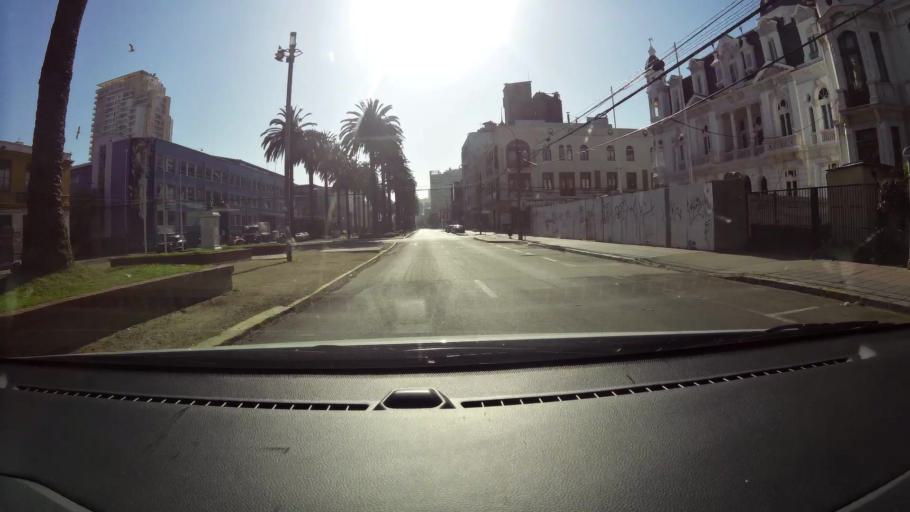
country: CL
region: Valparaiso
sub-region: Provincia de Valparaiso
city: Valparaiso
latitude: -33.0450
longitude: -71.6173
